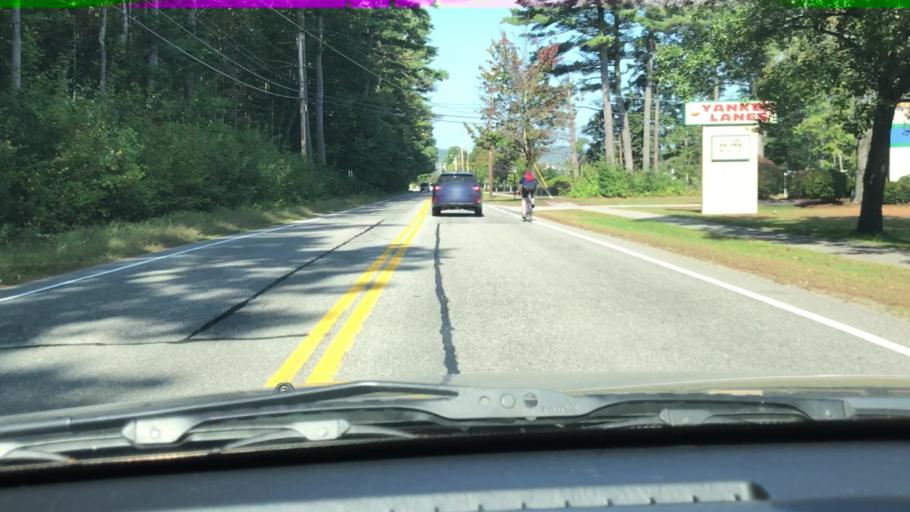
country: US
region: New Hampshire
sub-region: Cheshire County
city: Keene
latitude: 42.9452
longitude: -72.3152
